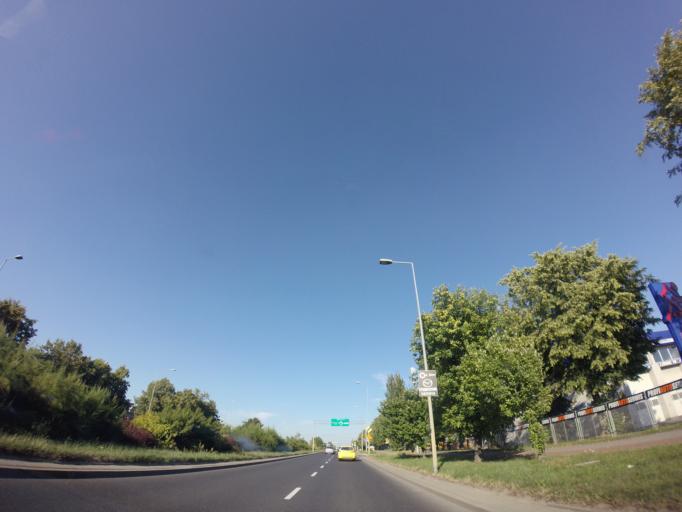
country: PL
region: Lubusz
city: Gorzow Wielkopolski
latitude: 52.7423
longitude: 15.2733
